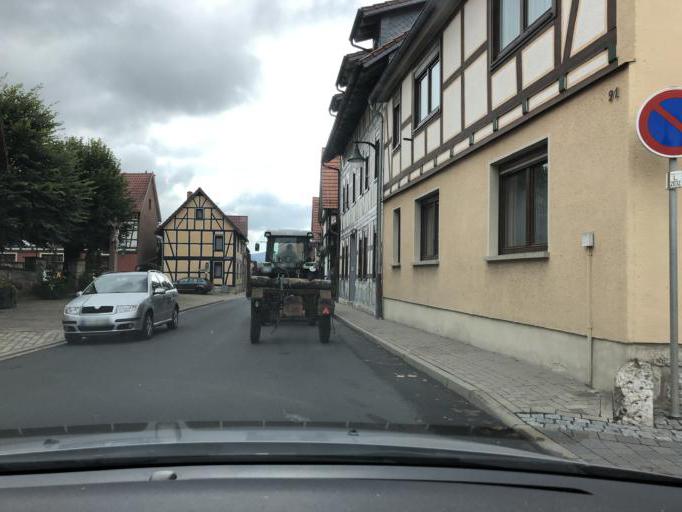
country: DE
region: Thuringia
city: Grossbartloff
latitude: 51.2505
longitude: 10.2111
